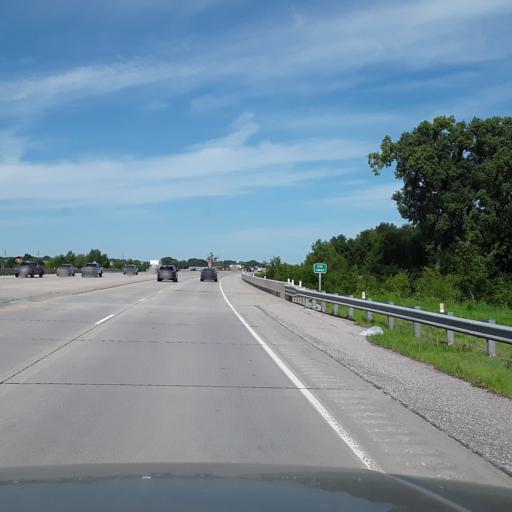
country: US
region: Nebraska
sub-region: Lancaster County
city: Lincoln
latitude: 40.8799
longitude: -96.7746
